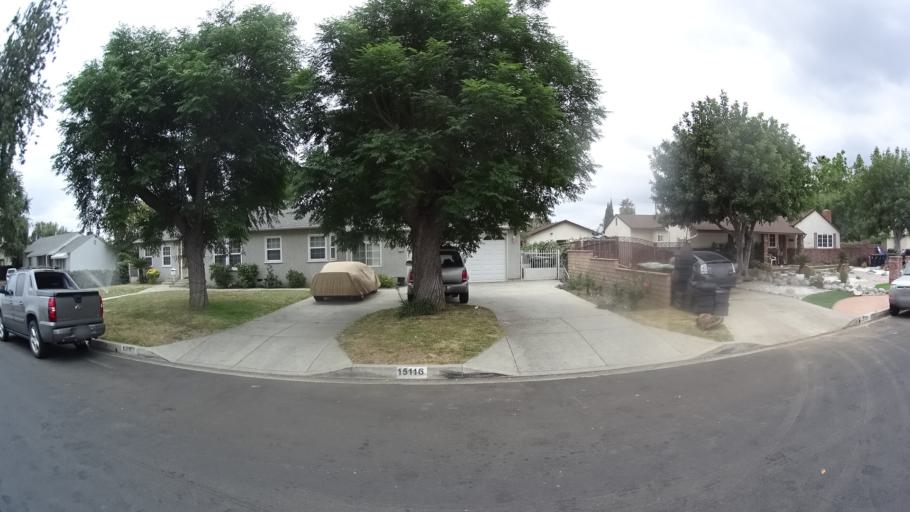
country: US
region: California
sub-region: Los Angeles County
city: San Fernando
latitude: 34.2621
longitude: -118.4619
